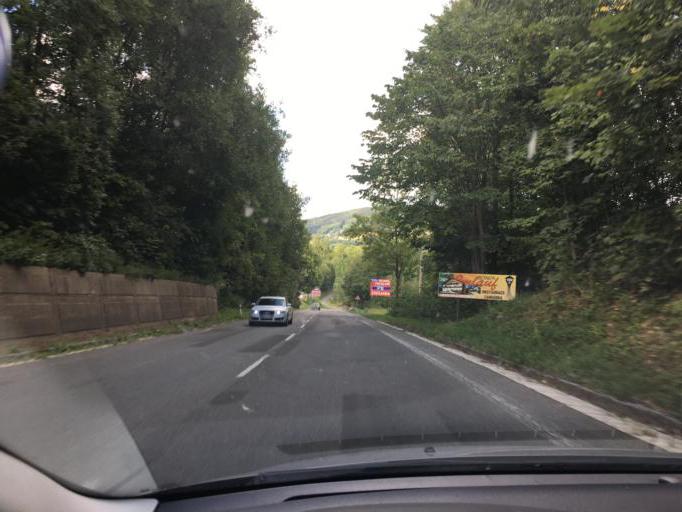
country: CZ
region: Kralovehradecky
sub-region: Okres Trutnov
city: Vrchlabi
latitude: 50.6345
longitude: 15.6035
